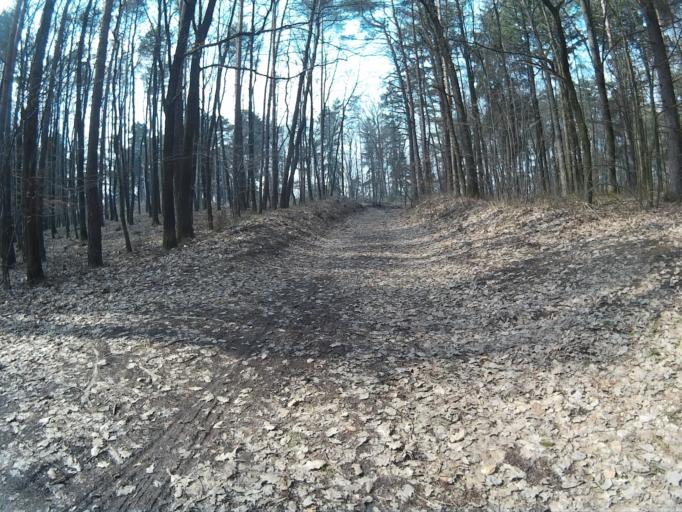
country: CZ
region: South Moravian
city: Pozorice
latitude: 49.2289
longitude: 16.7928
